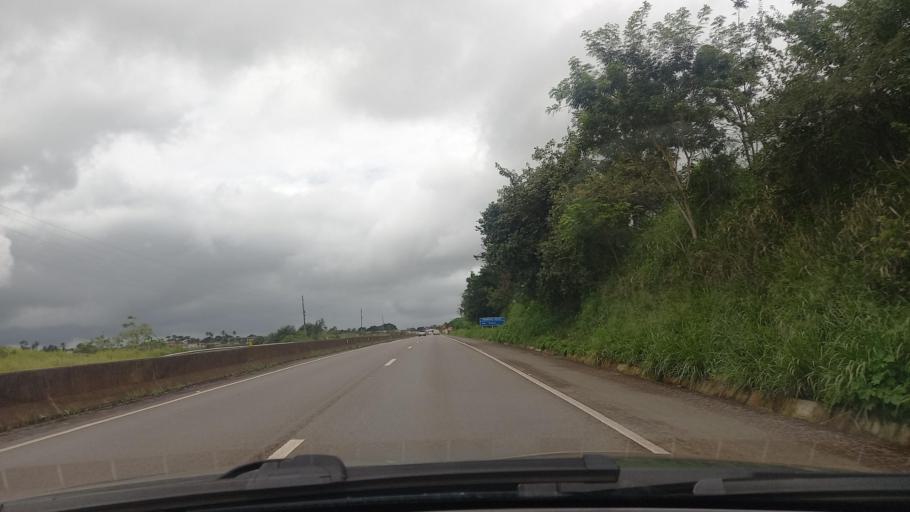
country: BR
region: Alagoas
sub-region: Limoeiro De Anadia
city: Limoeiro de Anadia
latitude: -9.7406
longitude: -36.4795
